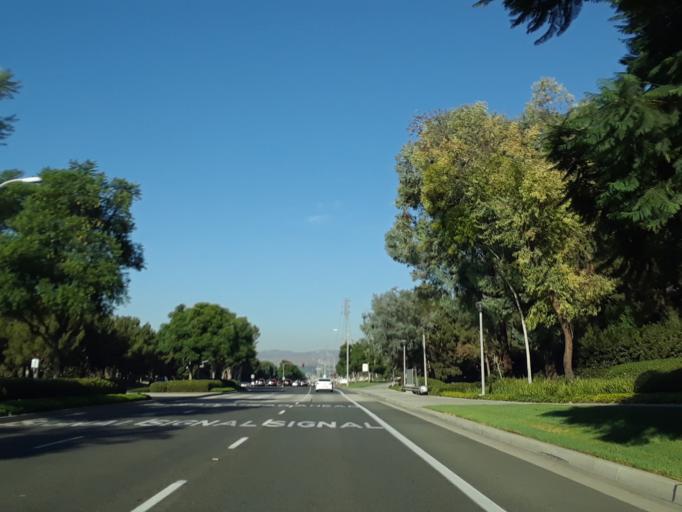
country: US
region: California
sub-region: Orange County
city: Irvine
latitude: 33.6719
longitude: -117.7862
